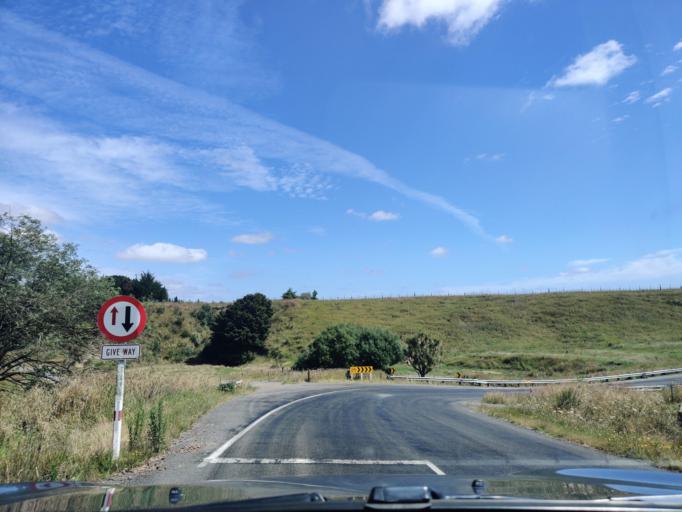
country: NZ
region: Manawatu-Wanganui
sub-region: Rangitikei District
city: Bulls
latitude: -40.1711
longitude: 175.4325
